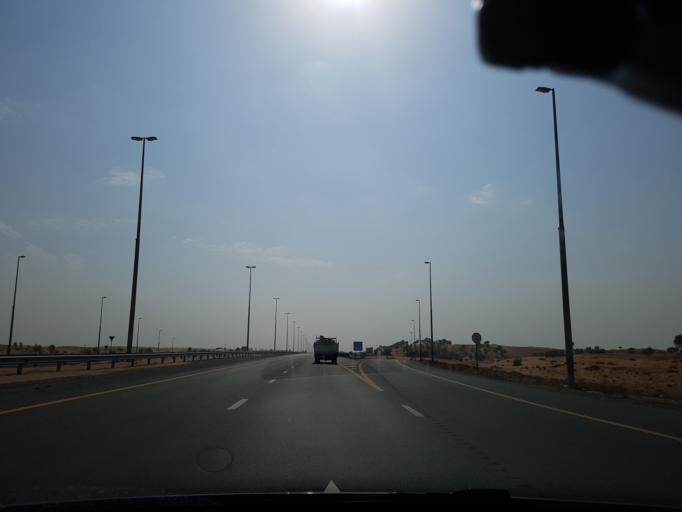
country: AE
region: Umm al Qaywayn
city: Umm al Qaywayn
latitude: 25.5168
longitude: 55.7490
